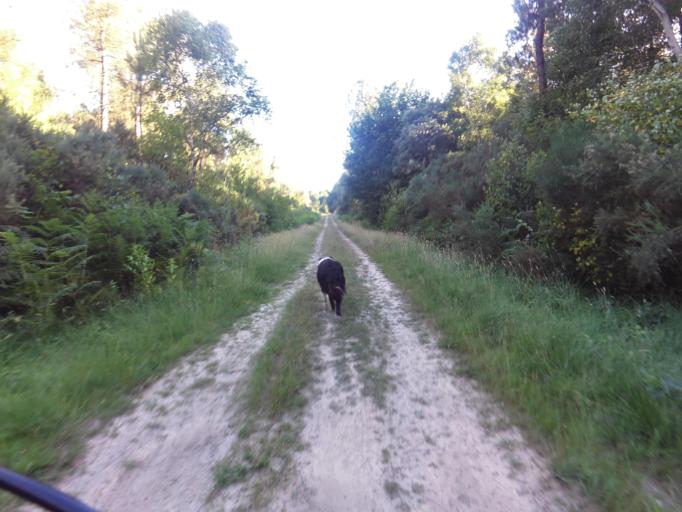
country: FR
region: Brittany
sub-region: Departement du Morbihan
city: Molac
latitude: 47.7559
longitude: -2.4107
